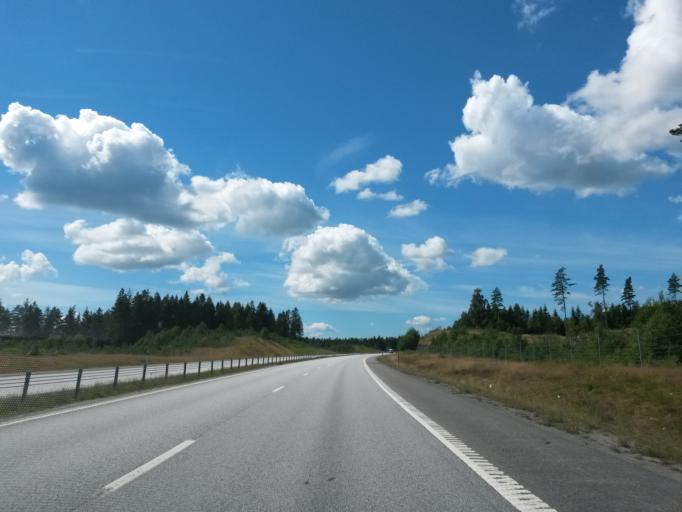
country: SE
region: Vaestra Goetaland
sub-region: Uddevalla Kommun
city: Uddevalla
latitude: 58.3294
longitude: 12.0493
